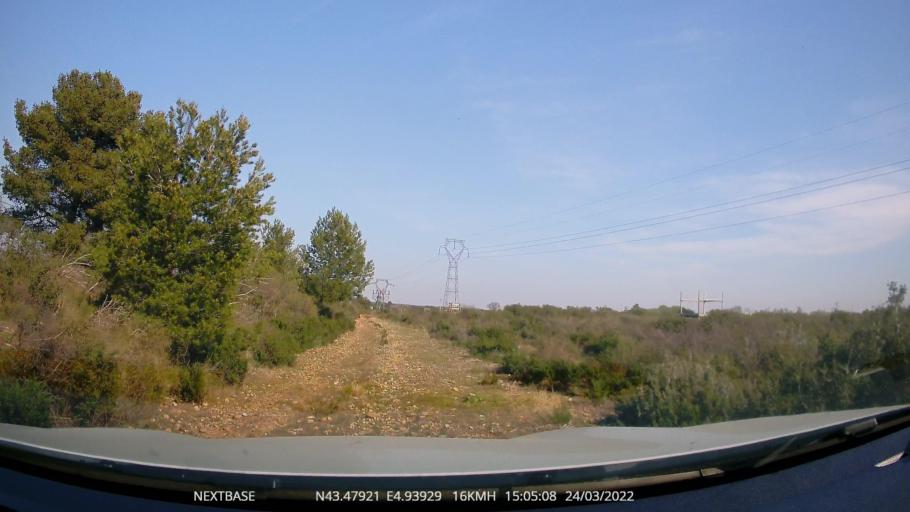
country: FR
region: Provence-Alpes-Cote d'Azur
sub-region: Departement des Bouches-du-Rhone
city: Fos-sur-Mer
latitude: 43.4794
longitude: 4.9392
